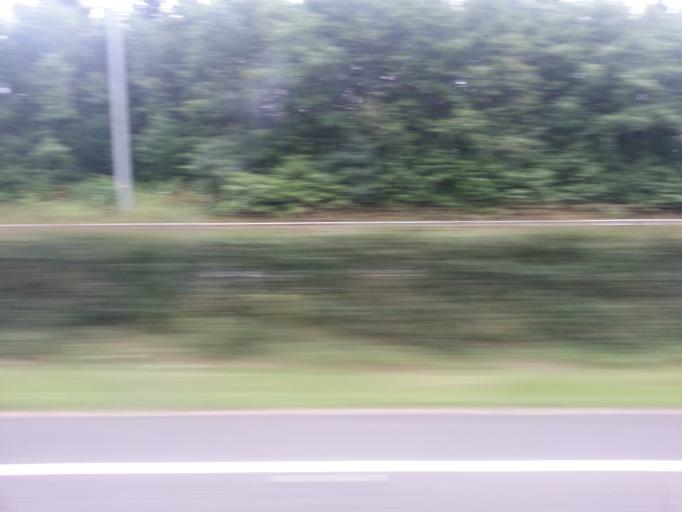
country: IE
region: Leinster
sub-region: Kildare
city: Naas
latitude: 53.2122
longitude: -6.7061
